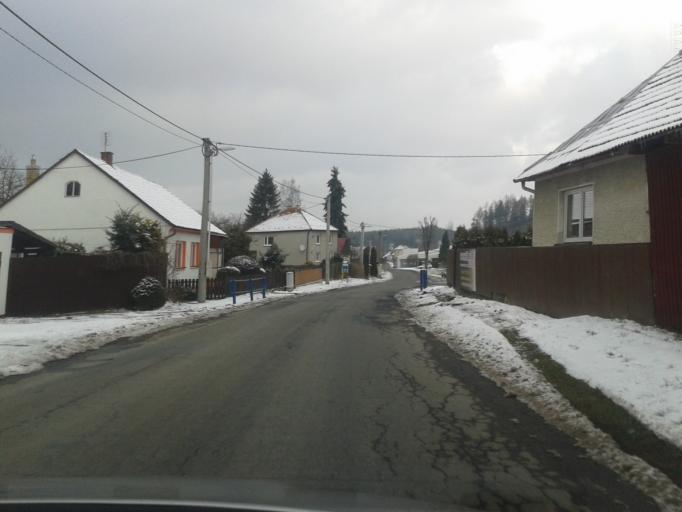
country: CZ
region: Olomoucky
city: Horni Stepanov
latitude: 49.5526
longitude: 16.7923
